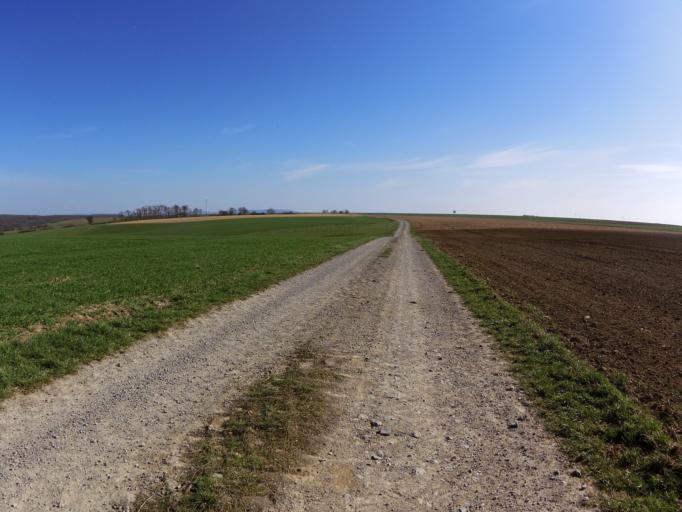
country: DE
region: Bavaria
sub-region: Regierungsbezirk Unterfranken
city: Prosselsheim
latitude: 49.8606
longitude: 10.1169
